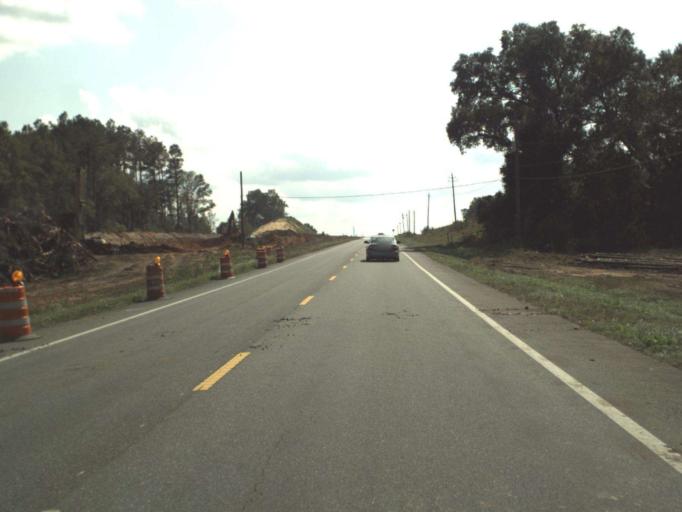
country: US
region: Florida
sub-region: Holmes County
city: Bonifay
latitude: 30.7109
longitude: -85.6859
